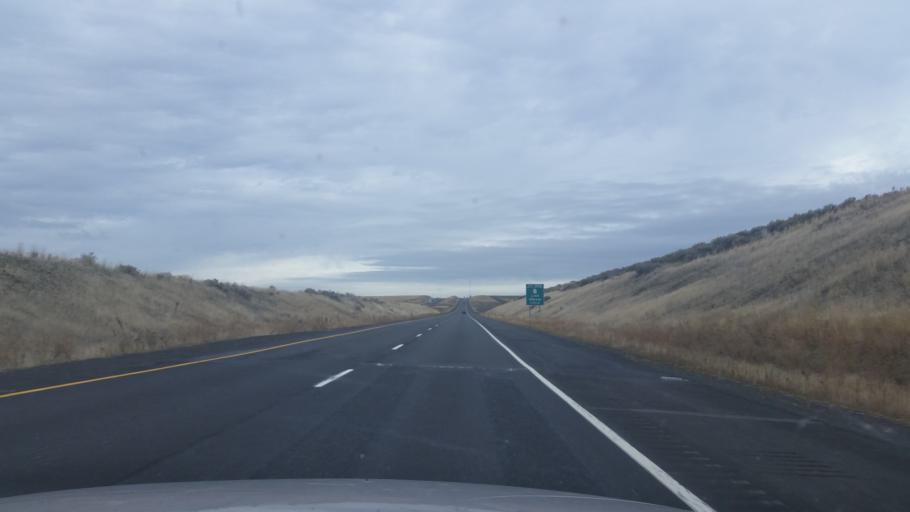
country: US
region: Washington
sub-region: Adams County
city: Ritzville
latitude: 47.0968
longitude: -118.6394
